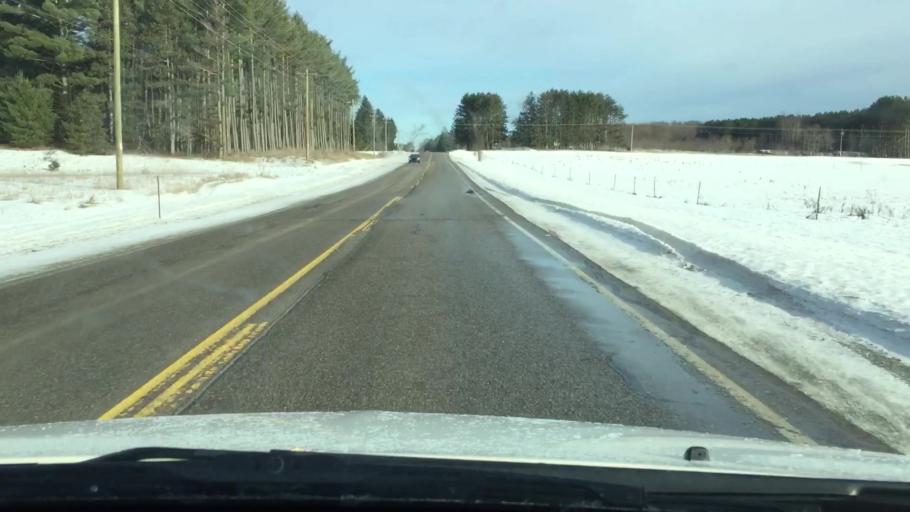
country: US
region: Michigan
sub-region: Kalkaska County
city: Kalkaska
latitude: 44.6409
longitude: -85.2546
